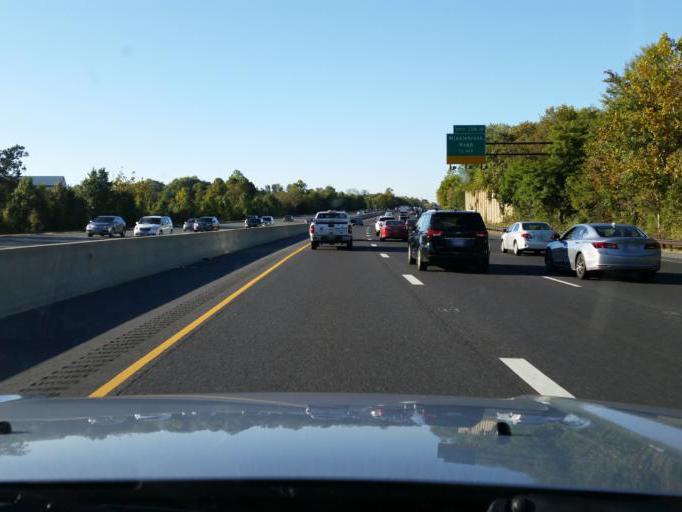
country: US
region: Maryland
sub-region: Montgomery County
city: Germantown
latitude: 39.1660
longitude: -77.2405
